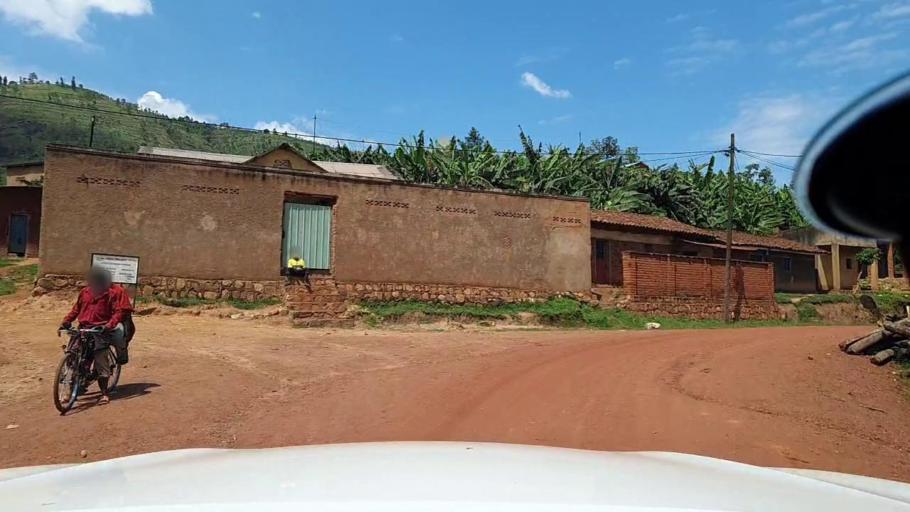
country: RW
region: Kigali
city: Kigali
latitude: -1.7920
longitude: 29.8846
